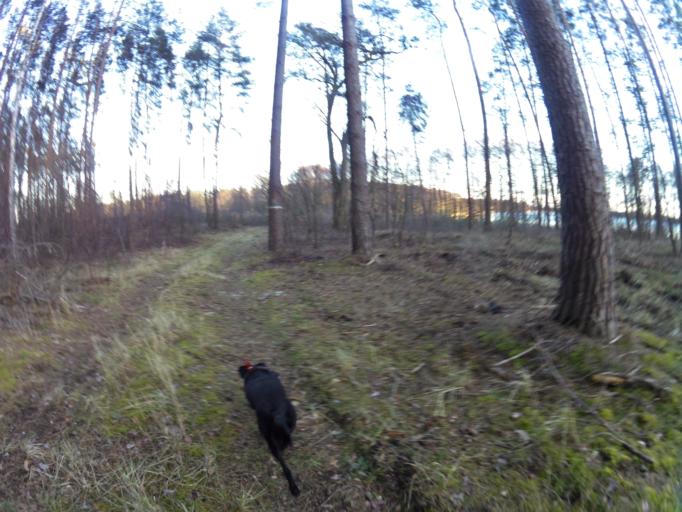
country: PL
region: West Pomeranian Voivodeship
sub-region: Powiat mysliborski
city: Debno
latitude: 52.8284
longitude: 14.7748
